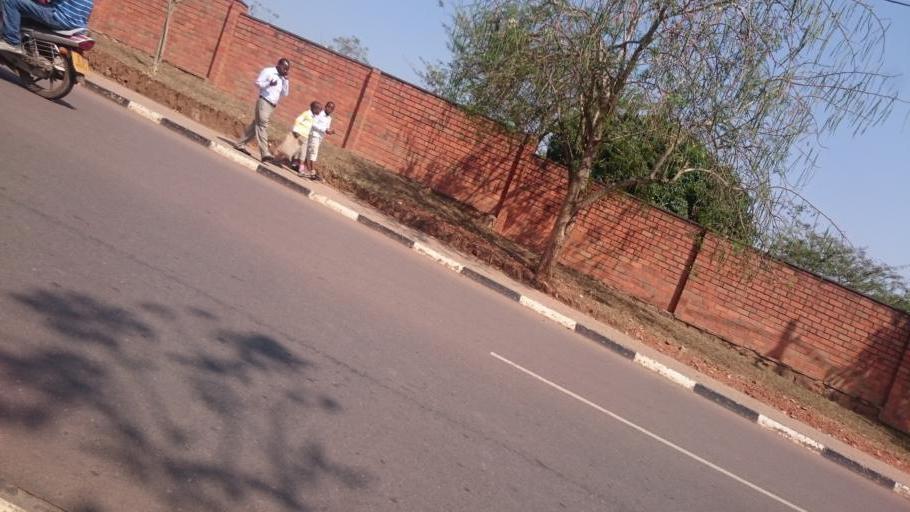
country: RW
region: Kigali
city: Kigali
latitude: -1.9433
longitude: 30.0883
